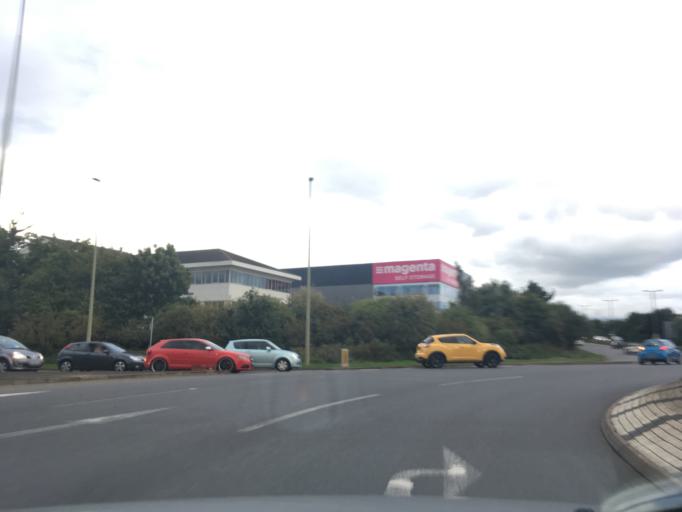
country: GB
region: England
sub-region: Oxfordshire
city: Banbury
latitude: 52.0723
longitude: -1.3196
